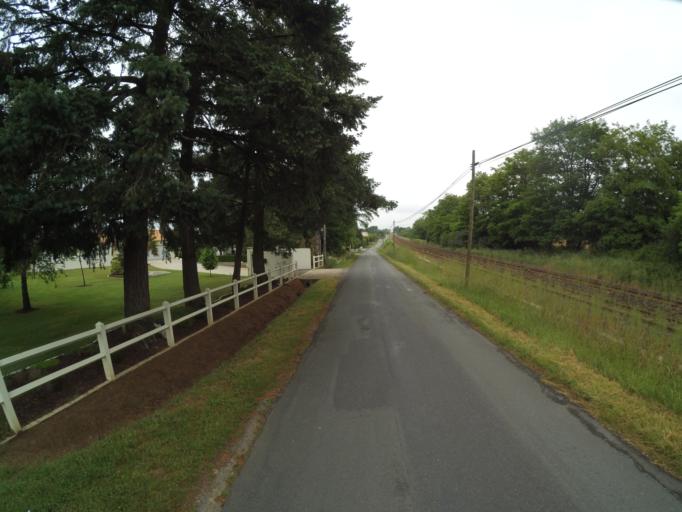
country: FR
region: Pays de la Loire
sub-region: Departement de la Vendee
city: La Roche-sur-Yon
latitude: 46.6401
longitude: -1.4330
